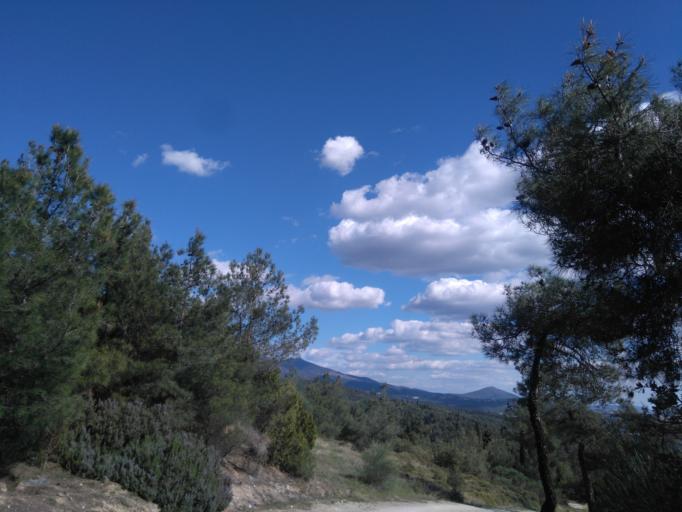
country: GR
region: Central Macedonia
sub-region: Nomos Thessalonikis
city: Agios Pavlos
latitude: 40.6359
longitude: 22.9794
